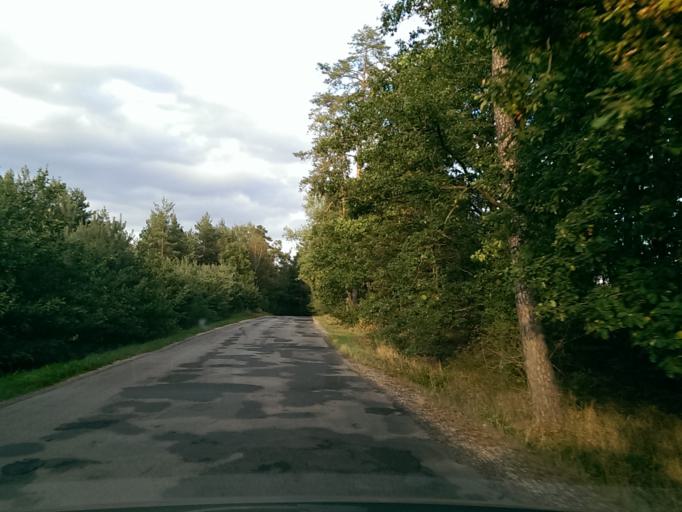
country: CZ
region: Central Bohemia
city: Dolni Bousov
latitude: 50.4951
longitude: 15.1160
